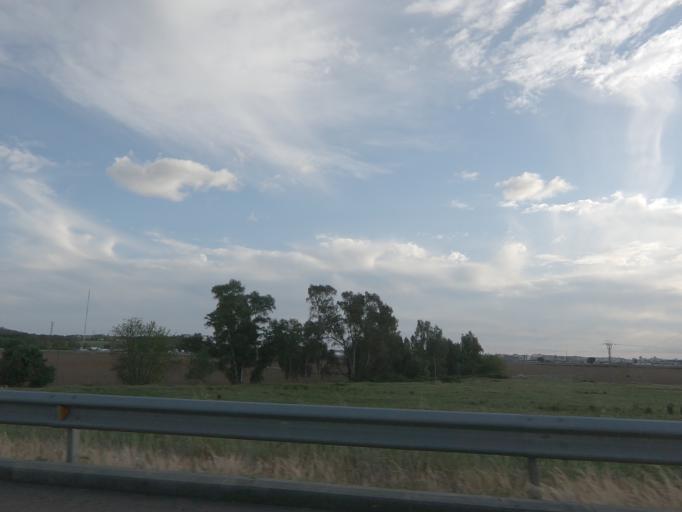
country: ES
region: Extremadura
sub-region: Provincia de Badajoz
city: Badajoz
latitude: 38.8952
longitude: -6.9223
